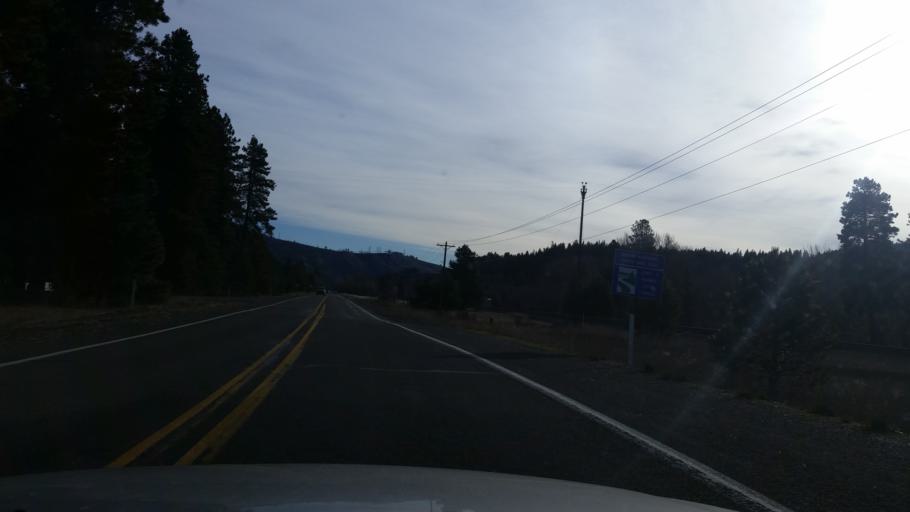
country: US
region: Washington
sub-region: Kittitas County
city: Cle Elum
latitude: 47.1742
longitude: -120.8540
